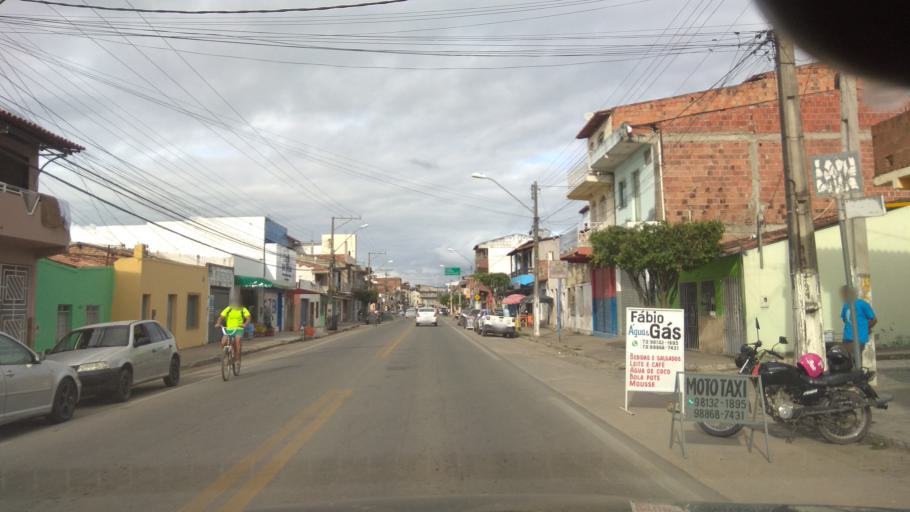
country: BR
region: Bahia
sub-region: Ipiau
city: Ipiau
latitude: -14.1353
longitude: -39.7444
